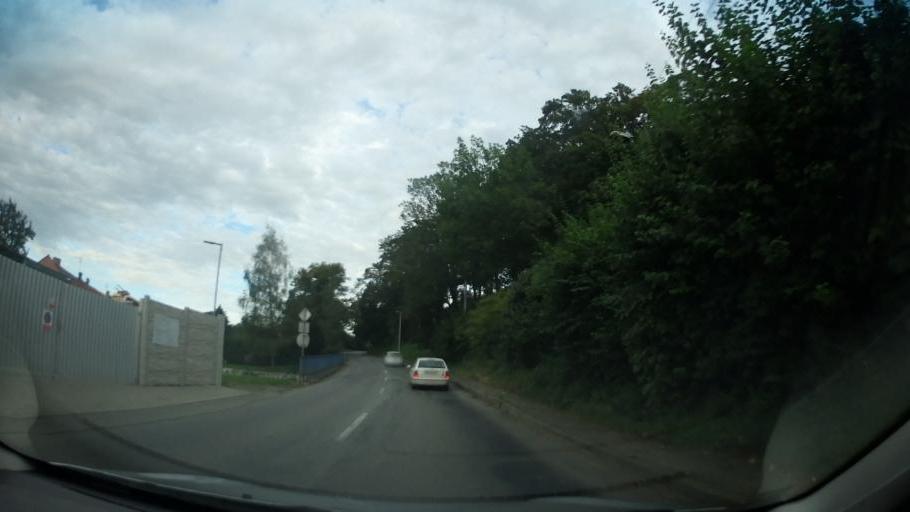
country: CZ
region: South Moravian
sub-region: Okres Blansko
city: Boskovice
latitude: 49.5391
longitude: 16.6984
